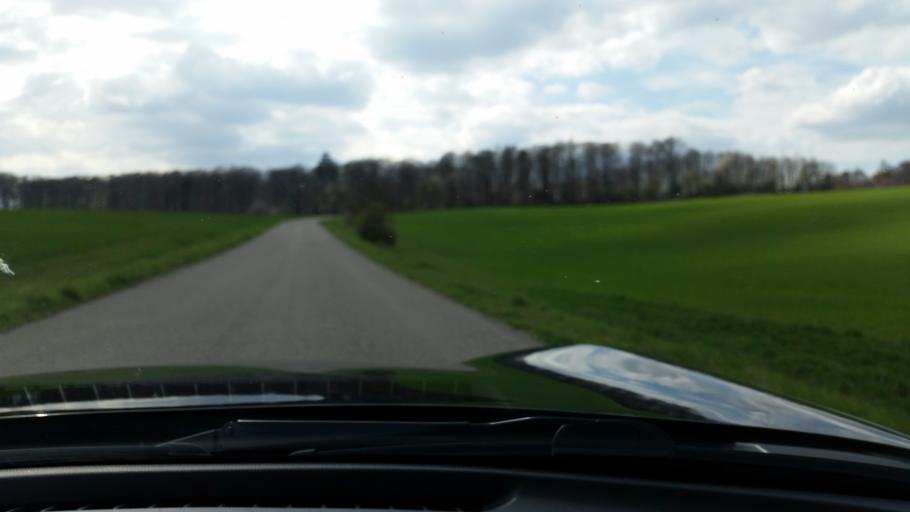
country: DE
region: Baden-Wuerttemberg
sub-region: Regierungsbezirk Stuttgart
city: Widdern
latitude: 49.3641
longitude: 9.4358
